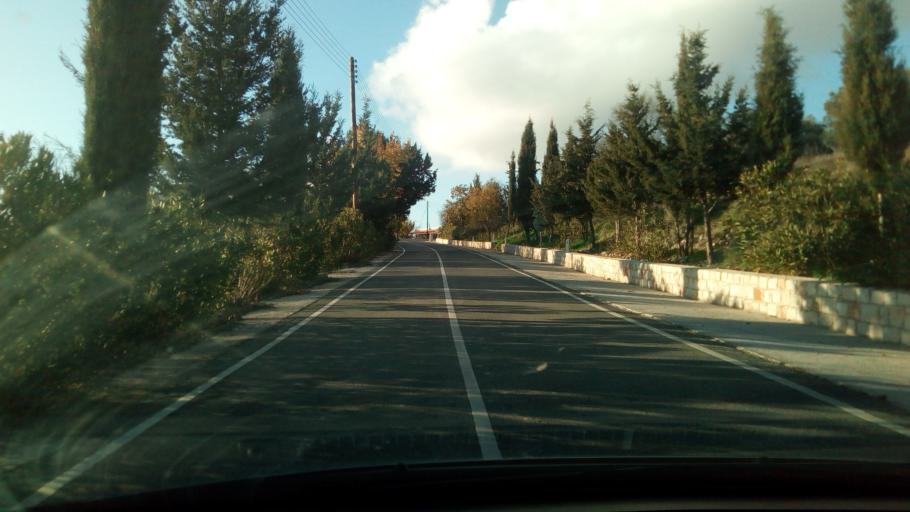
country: CY
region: Pafos
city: Tala
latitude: 34.9227
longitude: 32.5269
